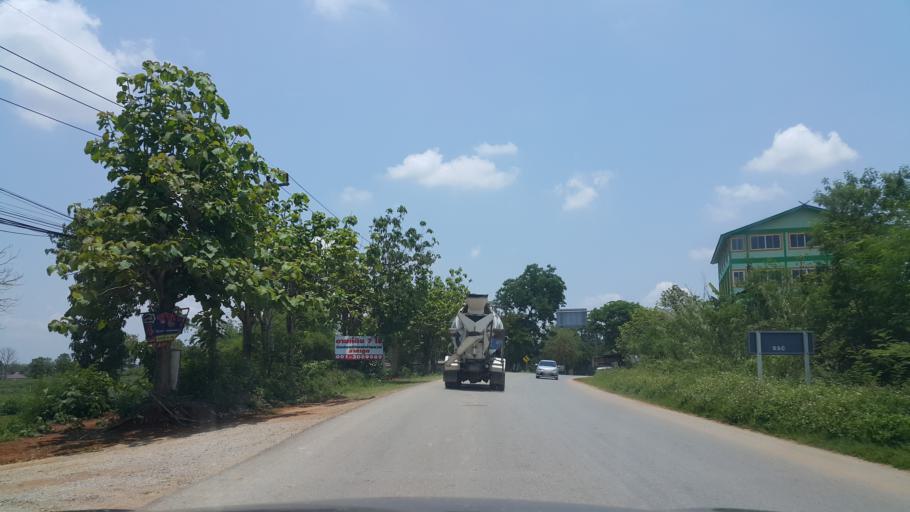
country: TH
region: Chiang Rai
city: Chiang Rai
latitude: 19.9364
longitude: 99.8110
